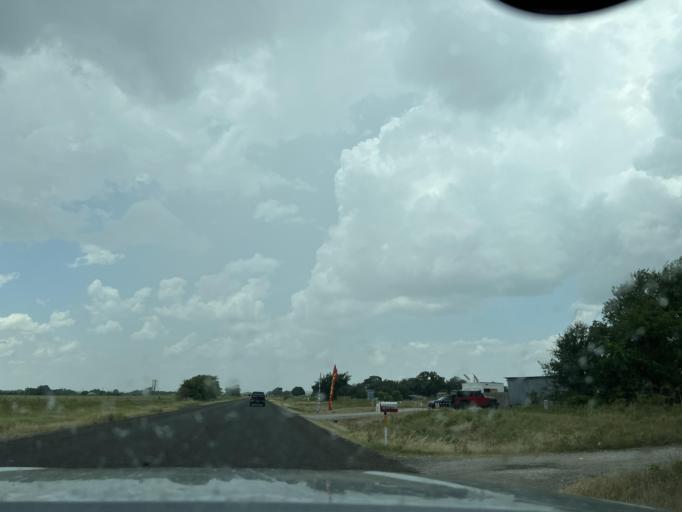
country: US
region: Texas
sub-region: Wise County
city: Boyd
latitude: 33.1451
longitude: -97.6387
